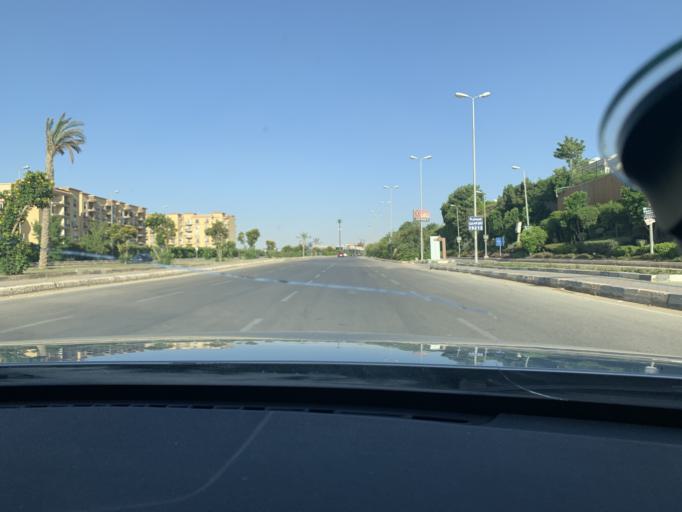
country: EG
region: Muhafazat al Qalyubiyah
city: Al Khankah
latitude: 30.0525
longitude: 31.5060
